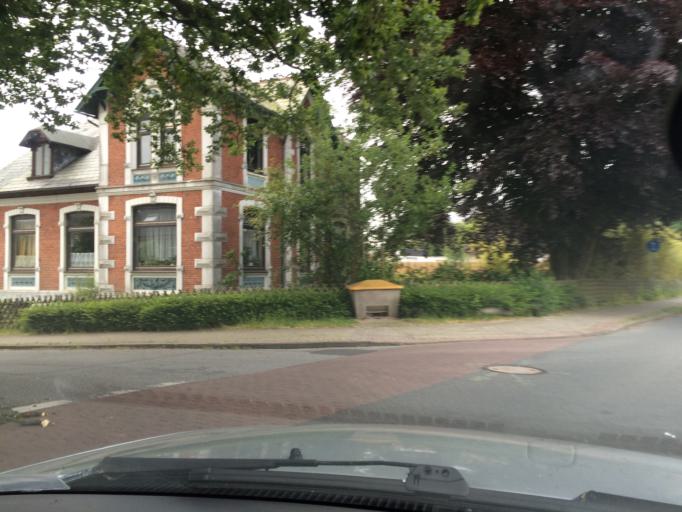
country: DE
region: Schleswig-Holstein
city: Oeversee
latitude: 54.6918
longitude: 9.4266
